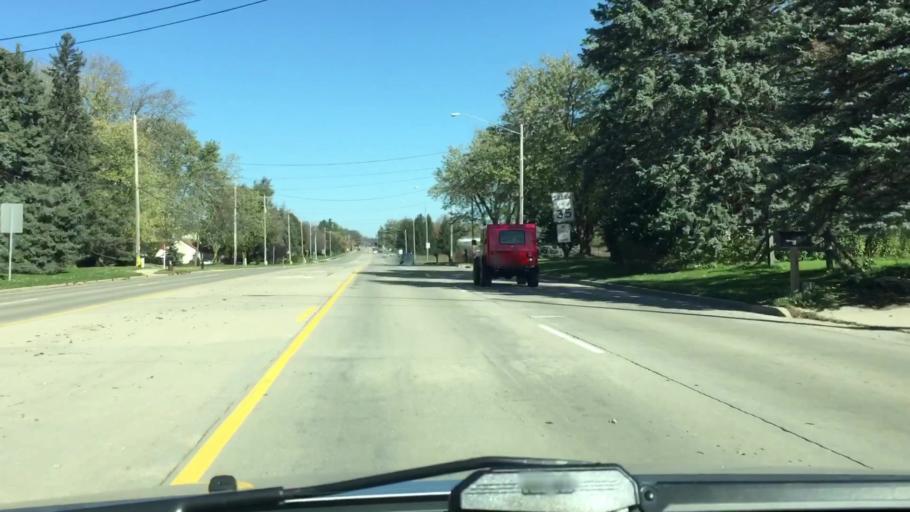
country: US
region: Wisconsin
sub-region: Waukesha County
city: Sussex
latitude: 43.1231
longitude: -88.2098
